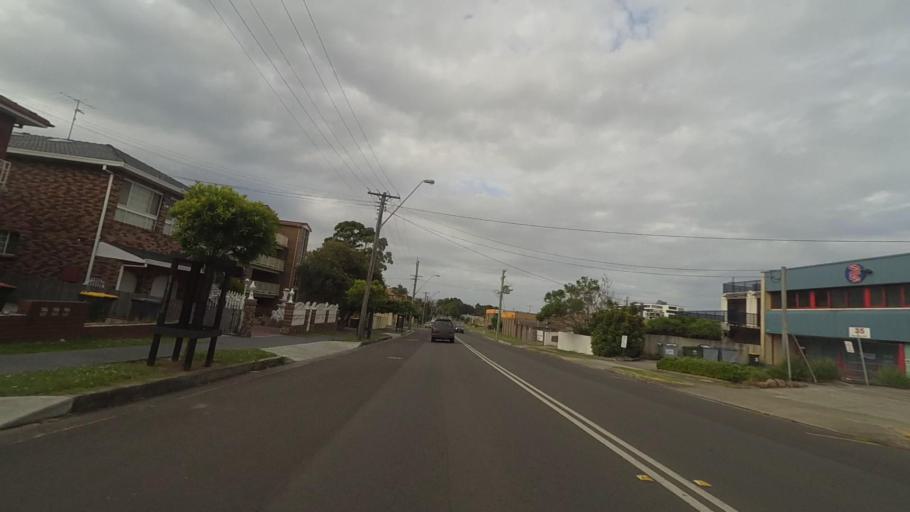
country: AU
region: New South Wales
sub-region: Wollongong
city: Wollongong
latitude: -34.4243
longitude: 150.8880
